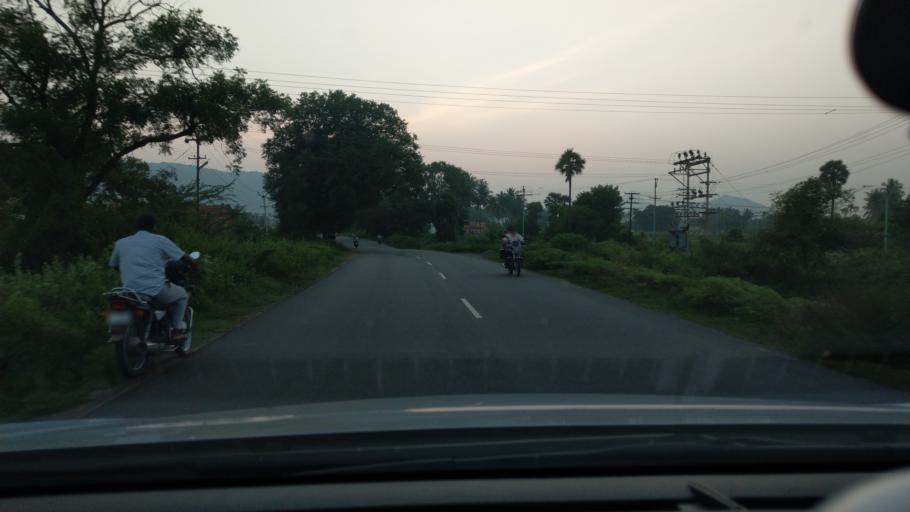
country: IN
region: Tamil Nadu
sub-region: Salem
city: Attur
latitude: 11.5957
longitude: 78.5705
